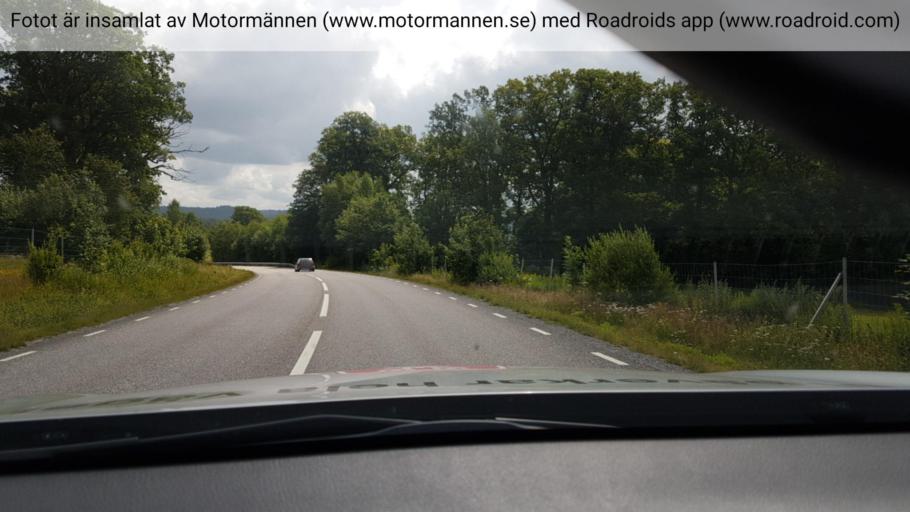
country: SE
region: Vaestra Goetaland
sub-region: Marks Kommun
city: Kinna
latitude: 57.4793
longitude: 12.6892
